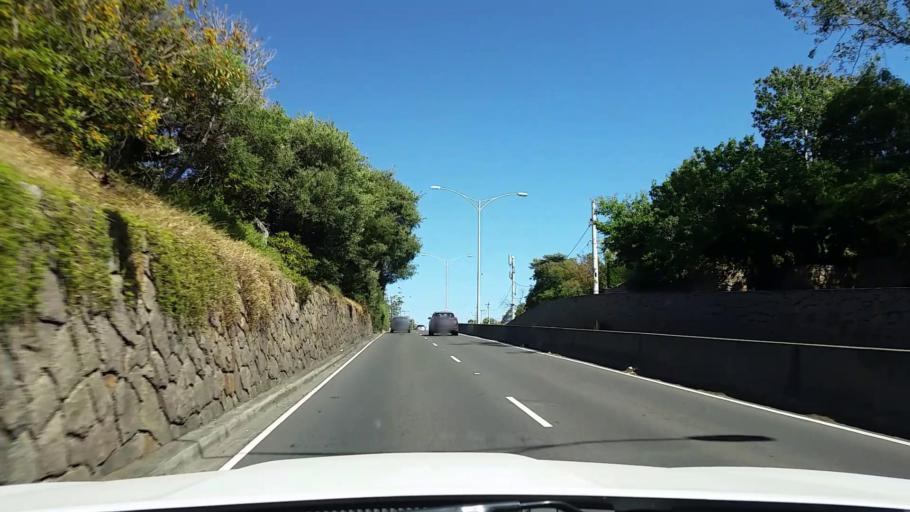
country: AU
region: Victoria
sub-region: Frankston
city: Frankston
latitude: -38.1564
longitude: 145.1058
